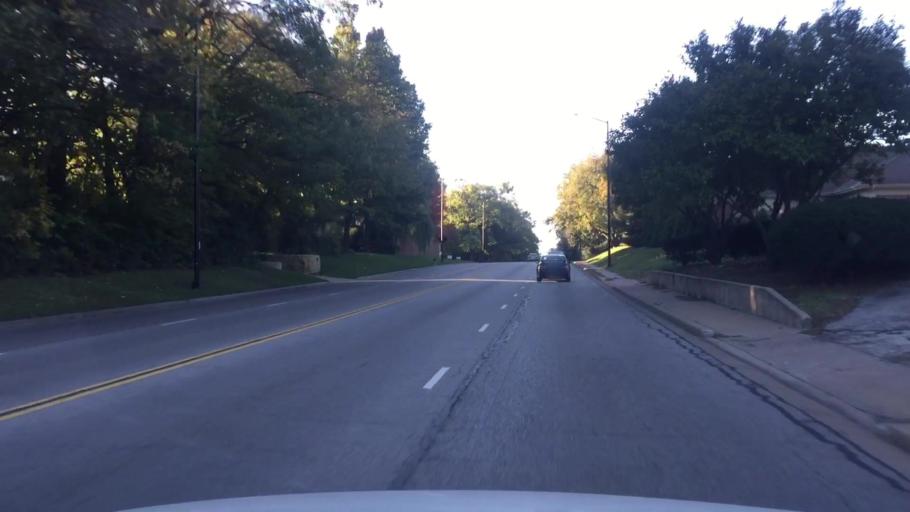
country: US
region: Kansas
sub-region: Johnson County
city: Mission
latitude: 39.0067
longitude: -94.6678
